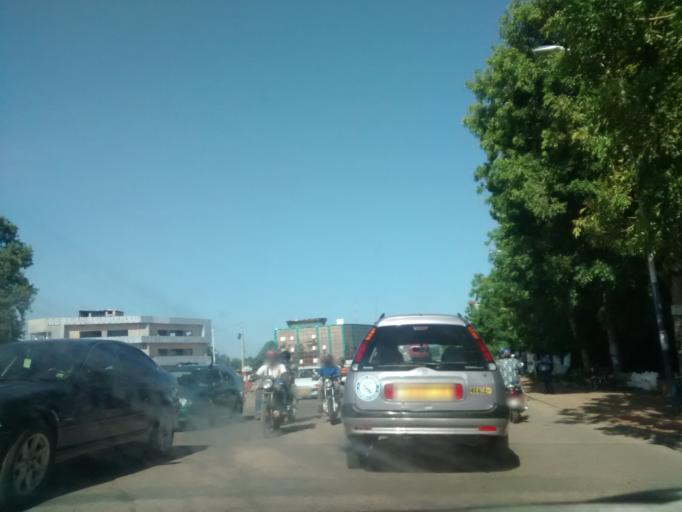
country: TG
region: Maritime
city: Lome
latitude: 6.1695
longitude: 1.1986
